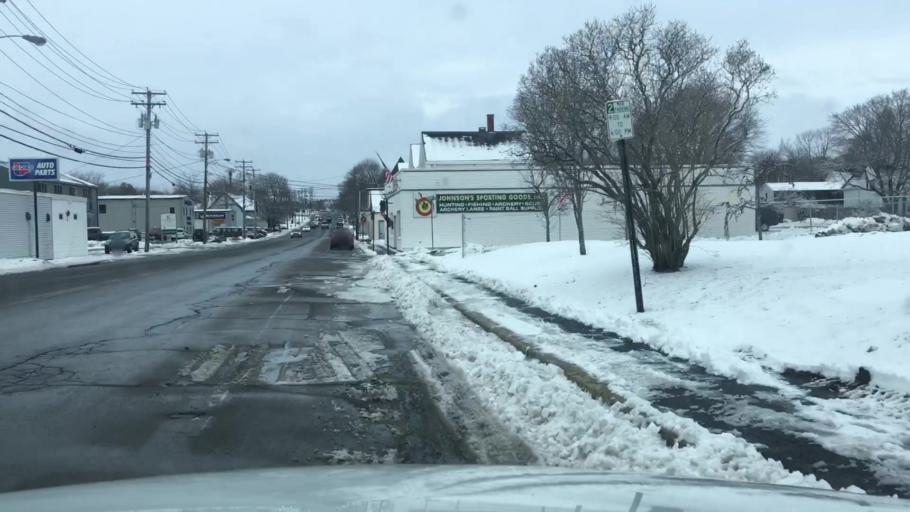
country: US
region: Maine
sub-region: Knox County
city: Rockland
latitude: 44.1021
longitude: -69.1115
